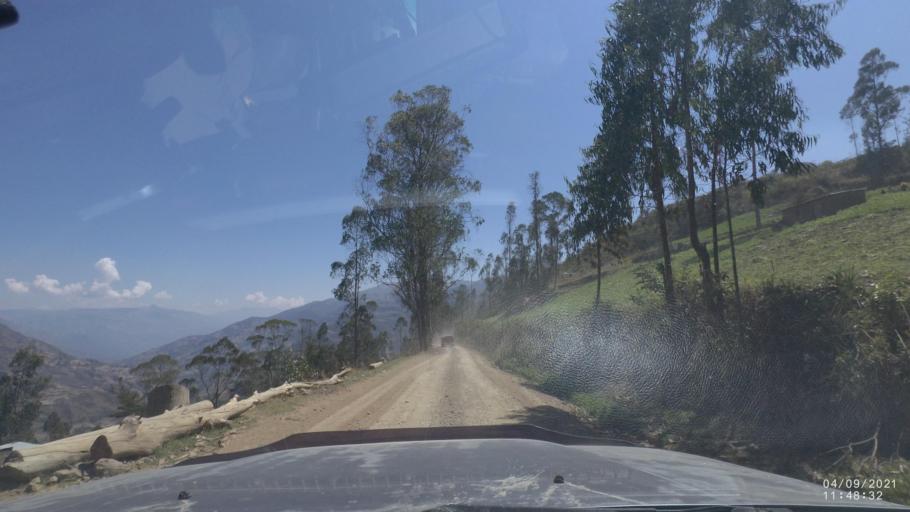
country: BO
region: Cochabamba
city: Colchani
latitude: -17.2246
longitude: -66.5244
